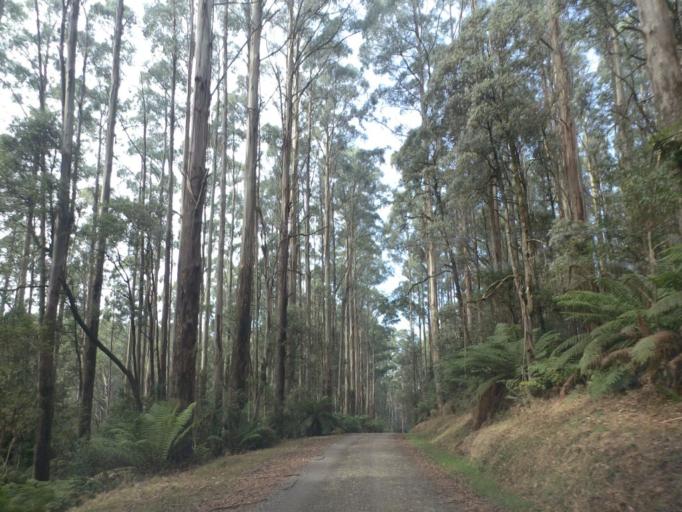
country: AU
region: Victoria
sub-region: Yarra Ranges
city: Healesville
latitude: -37.5702
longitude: 145.5423
